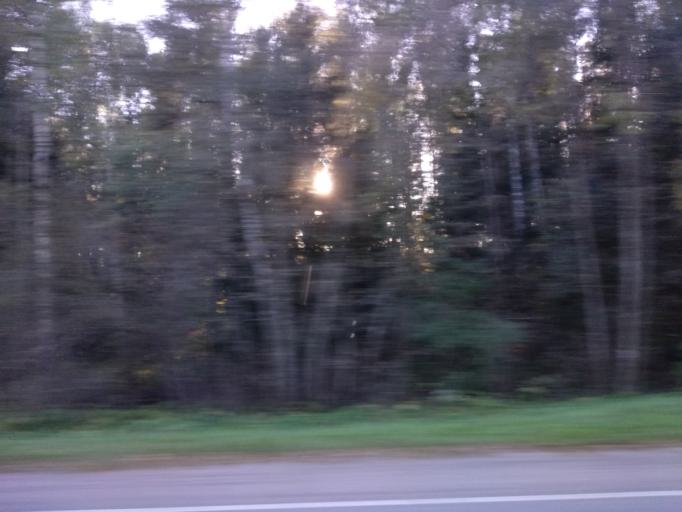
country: EE
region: Polvamaa
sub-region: Polva linn
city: Polva
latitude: 58.0477
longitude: 27.0644
